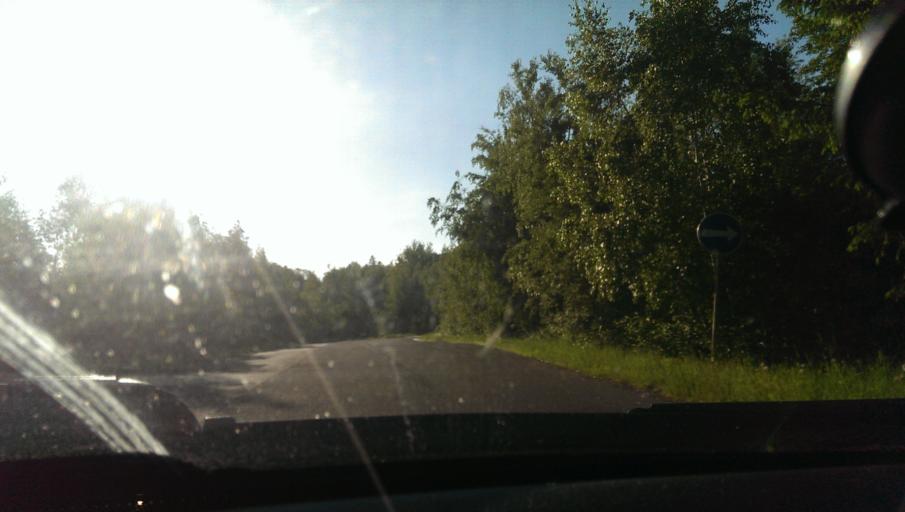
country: CZ
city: Ticha
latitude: 49.5518
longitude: 18.2332
